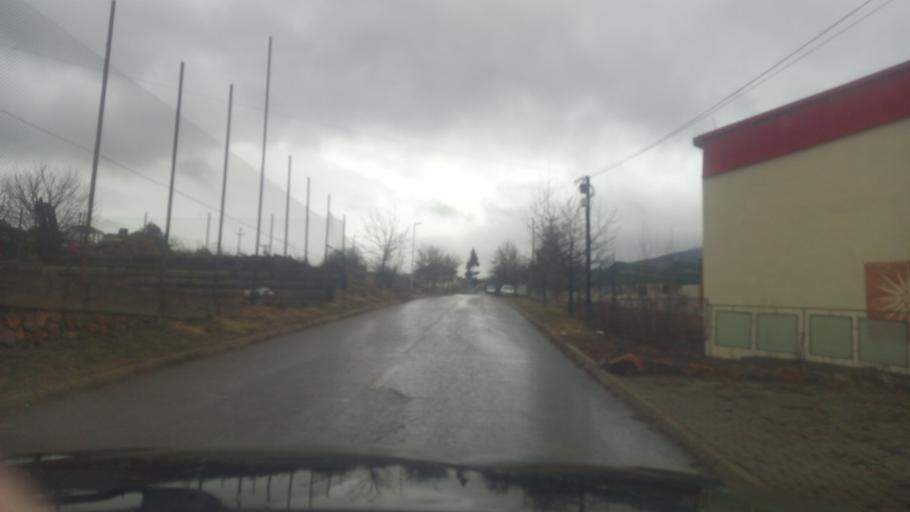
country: MK
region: Pehcevo
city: Pehcevo
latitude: 41.7623
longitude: 22.8815
